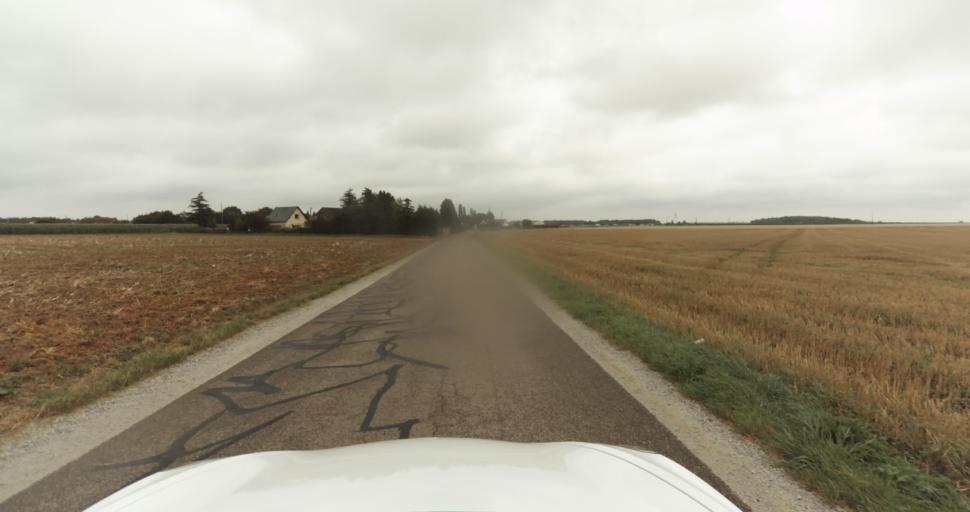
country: FR
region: Haute-Normandie
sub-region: Departement de l'Eure
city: Aviron
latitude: 49.0690
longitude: 1.1116
